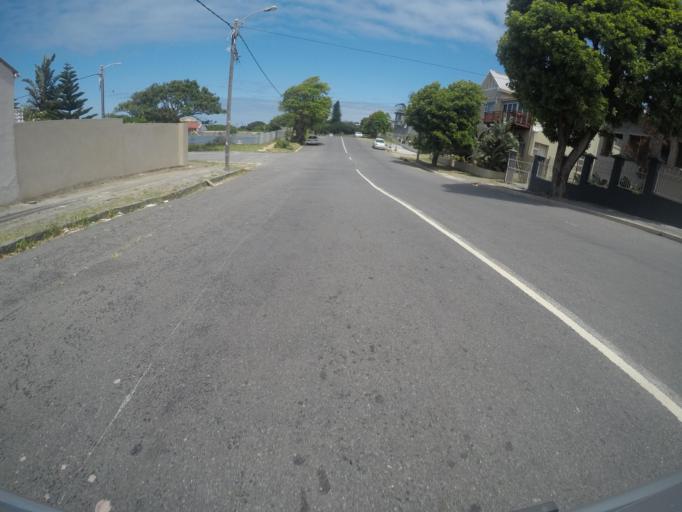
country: ZA
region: Eastern Cape
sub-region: Buffalo City Metropolitan Municipality
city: East London
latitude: -33.0201
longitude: 27.9113
